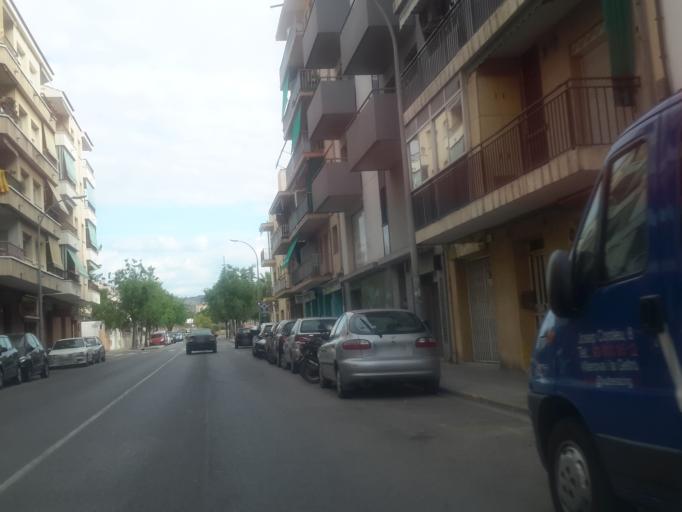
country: ES
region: Catalonia
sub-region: Provincia de Barcelona
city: Vilanova i la Geltru
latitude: 41.2253
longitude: 1.7163
